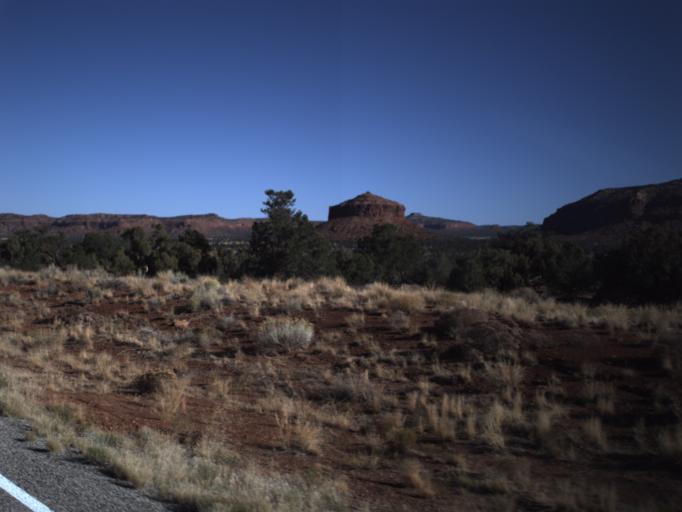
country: US
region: Utah
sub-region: San Juan County
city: Blanding
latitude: 37.6294
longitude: -110.0882
